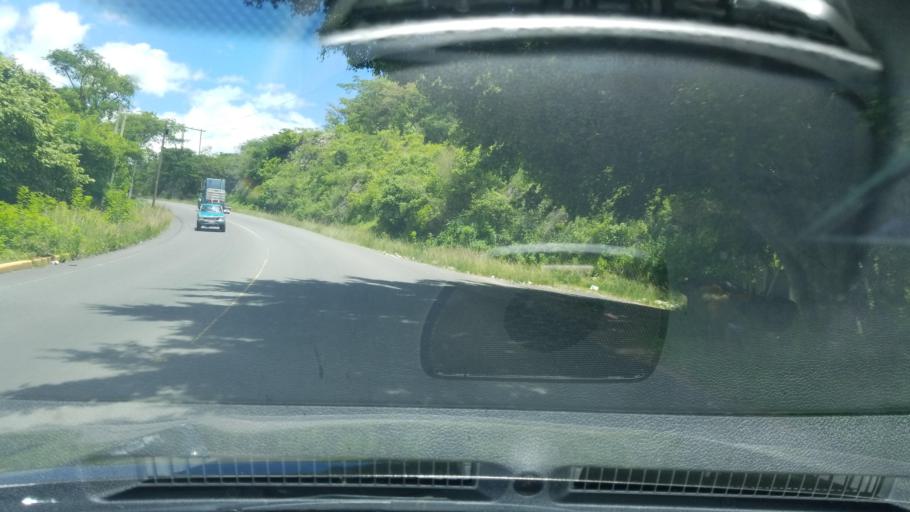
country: HN
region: Francisco Morazan
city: Rio Abajo
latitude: 14.1814
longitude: -87.2048
